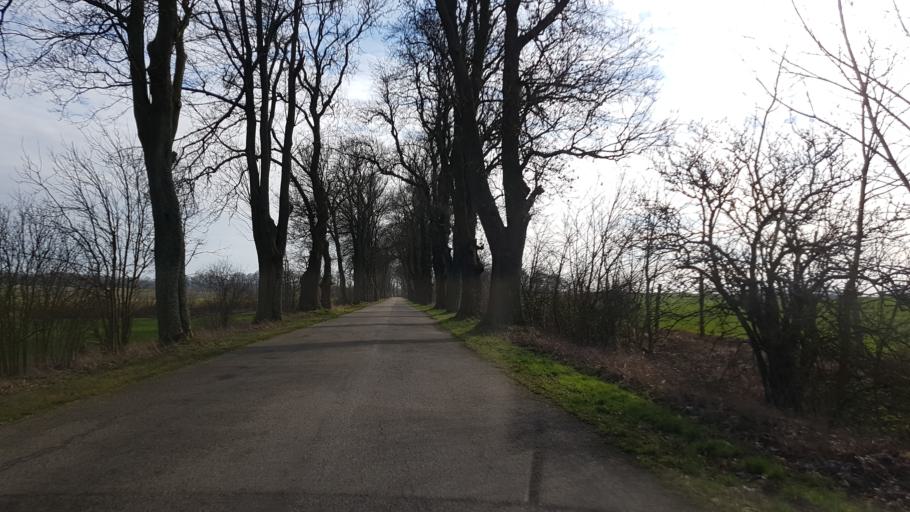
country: PL
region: West Pomeranian Voivodeship
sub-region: Powiat policki
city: Dobra
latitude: 53.5479
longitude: 14.3100
